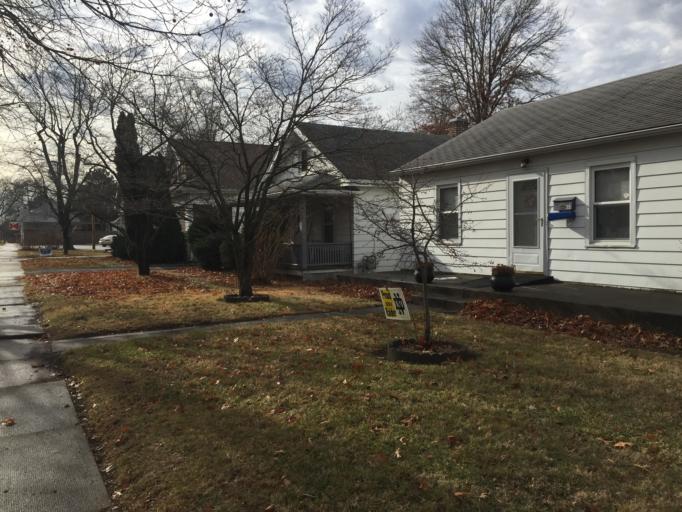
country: US
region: Illinois
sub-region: Adams County
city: Quincy
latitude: 39.9442
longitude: -91.3872
